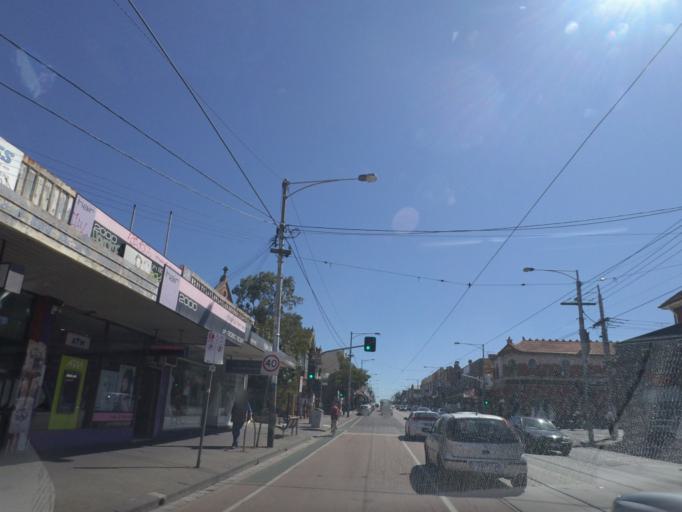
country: AU
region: Victoria
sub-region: Moreland
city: Brunswick
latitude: -37.7658
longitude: 144.9622
